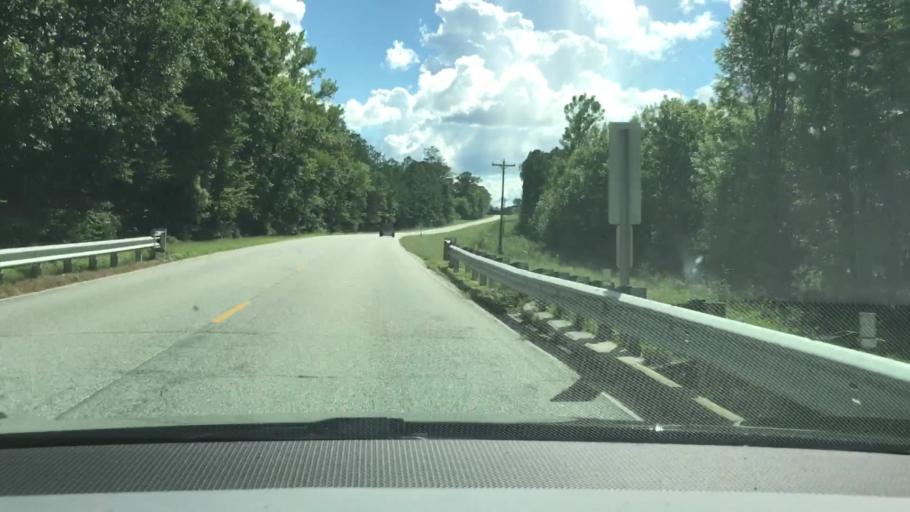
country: US
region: Alabama
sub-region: Montgomery County
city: Pike Road
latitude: 32.2022
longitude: -86.1025
